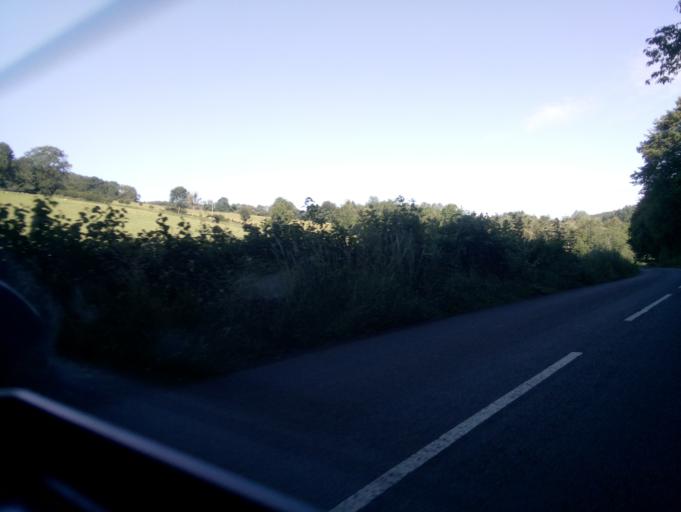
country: GB
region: England
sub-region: Gloucestershire
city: Coleford
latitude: 51.7913
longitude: -2.6567
